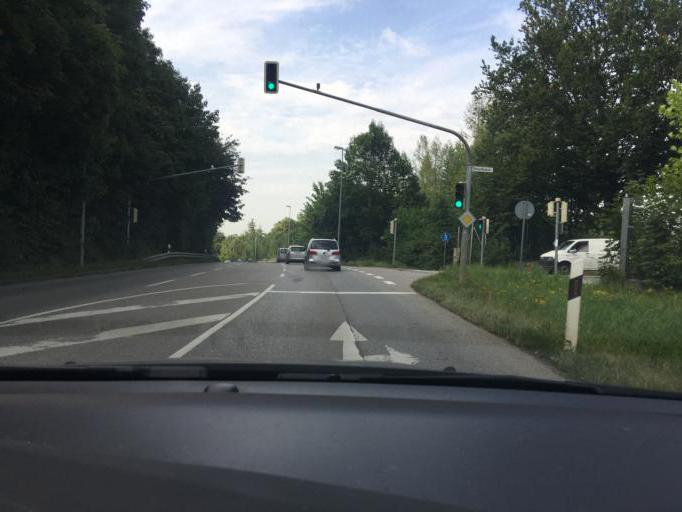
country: DE
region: Bavaria
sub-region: Upper Bavaria
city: Erding
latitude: 48.3068
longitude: 11.9190
